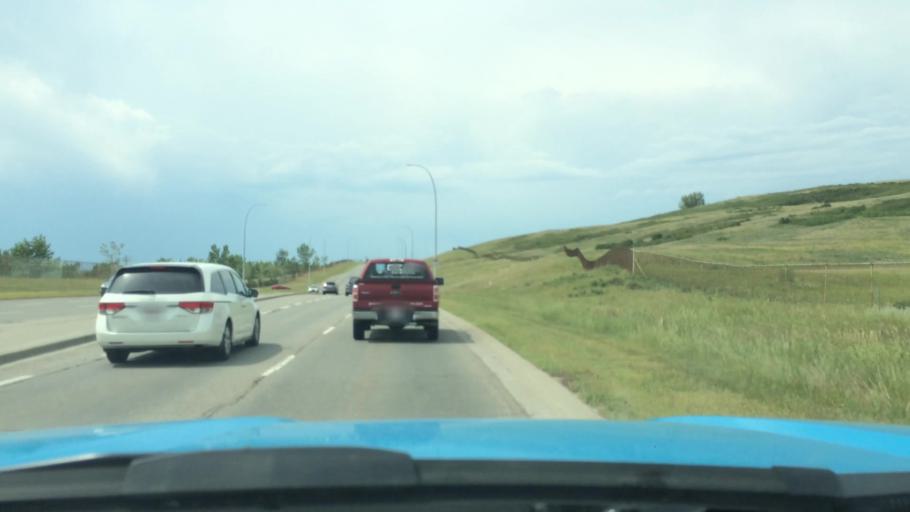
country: CA
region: Alberta
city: Calgary
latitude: 51.0922
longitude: -114.1035
